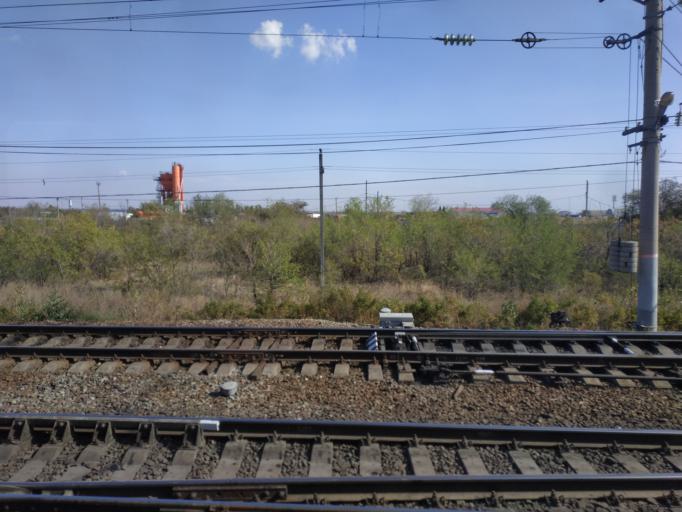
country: RU
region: Volgograd
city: Gumrak
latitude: 48.7915
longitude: 44.3668
